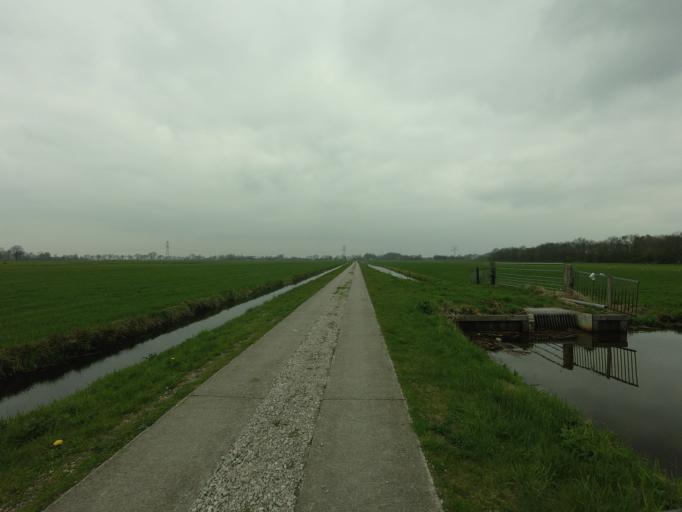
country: NL
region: Utrecht
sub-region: Gemeente De Bilt
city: De Bilt
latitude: 52.1411
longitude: 5.1520
